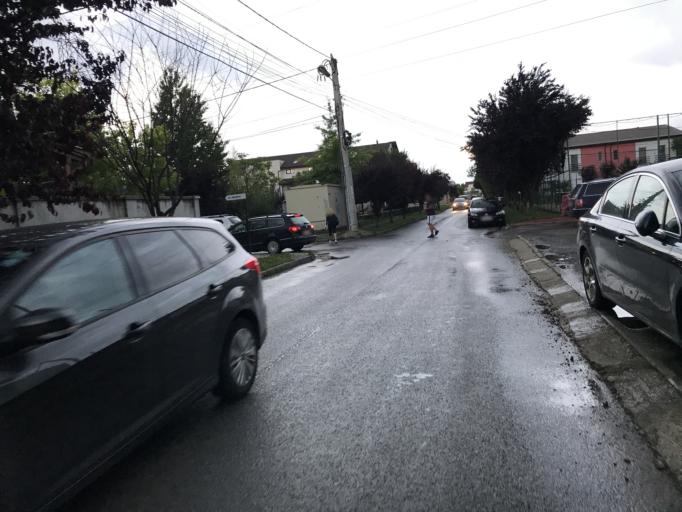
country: RO
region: Timis
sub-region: Comuna Dumbravita
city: Dumbravita
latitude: 45.7883
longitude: 21.2334
